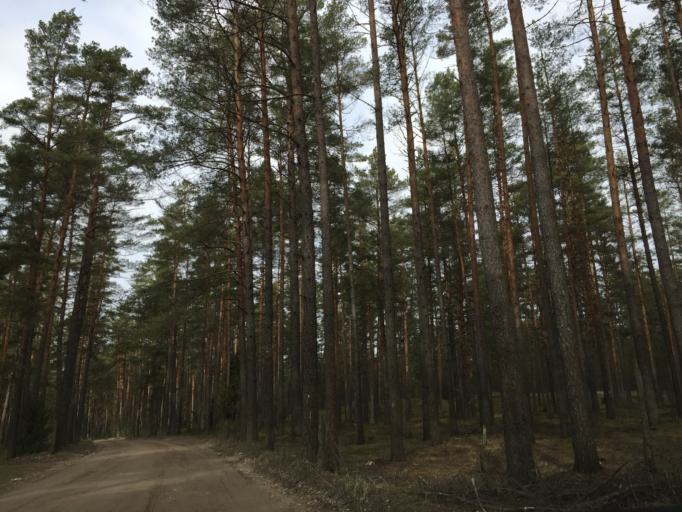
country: LV
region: Garkalne
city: Garkalne
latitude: 57.0668
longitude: 24.4693
